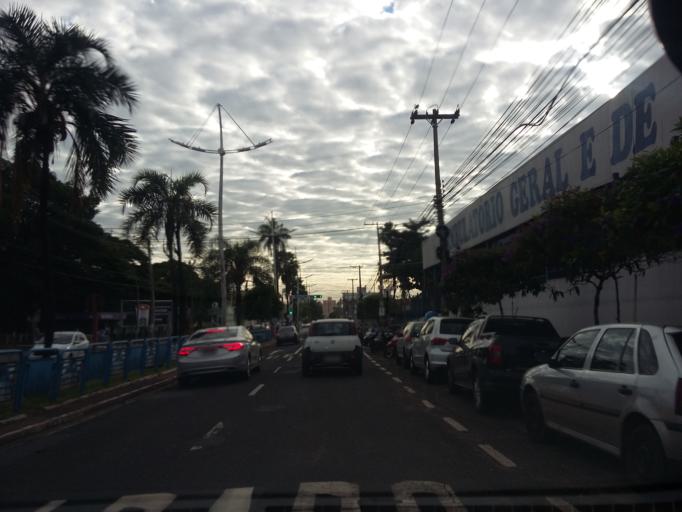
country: BR
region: Sao Paulo
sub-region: Sao Jose Do Rio Preto
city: Sao Jose do Rio Preto
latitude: -20.8288
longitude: -49.3967
